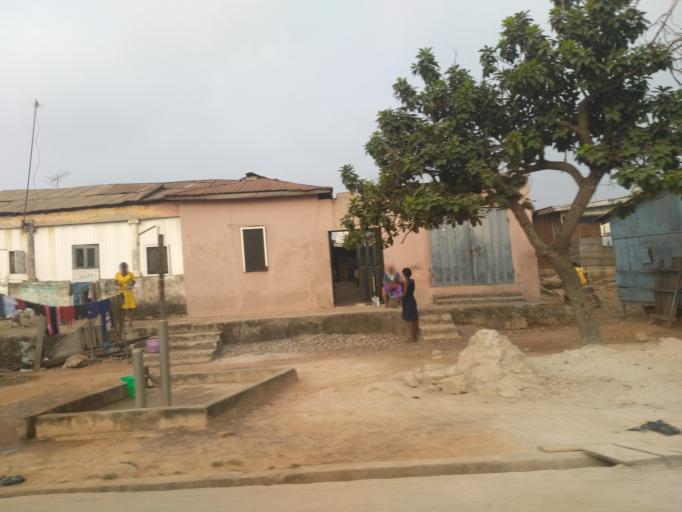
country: GH
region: Ashanti
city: Kumasi
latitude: 6.6853
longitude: -1.5903
